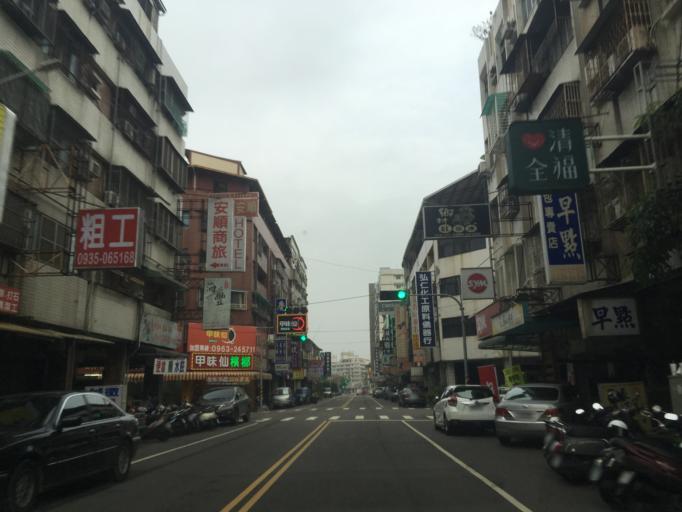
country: TW
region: Taiwan
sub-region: Taichung City
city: Taichung
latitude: 24.1767
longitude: 120.6793
